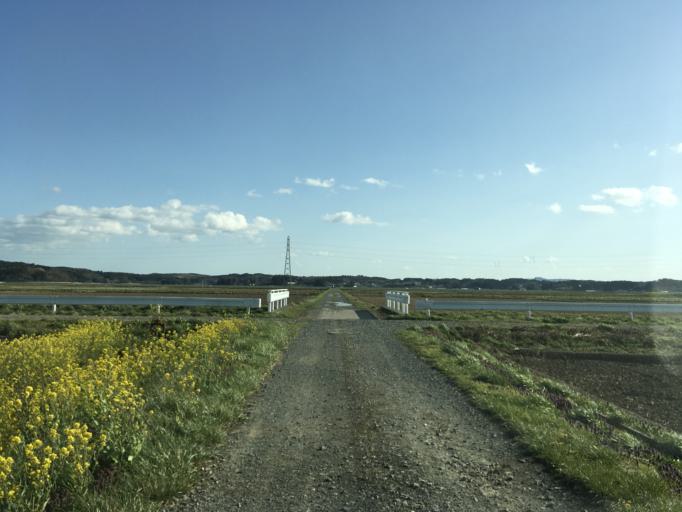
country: JP
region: Miyagi
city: Wakuya
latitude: 38.6589
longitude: 141.2412
